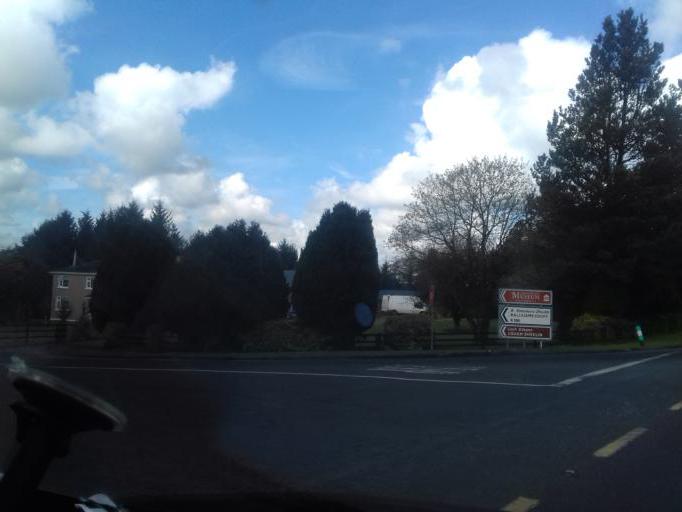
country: IE
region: Ulster
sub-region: An Cabhan
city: Ballyjamesduff
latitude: 53.9018
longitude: -7.1776
